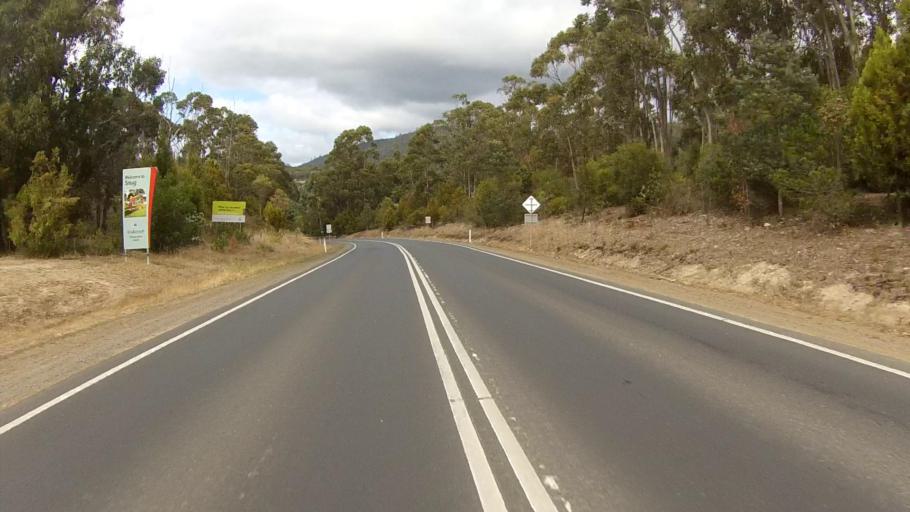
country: AU
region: Tasmania
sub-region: Kingborough
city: Margate
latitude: -43.0612
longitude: 147.2542
